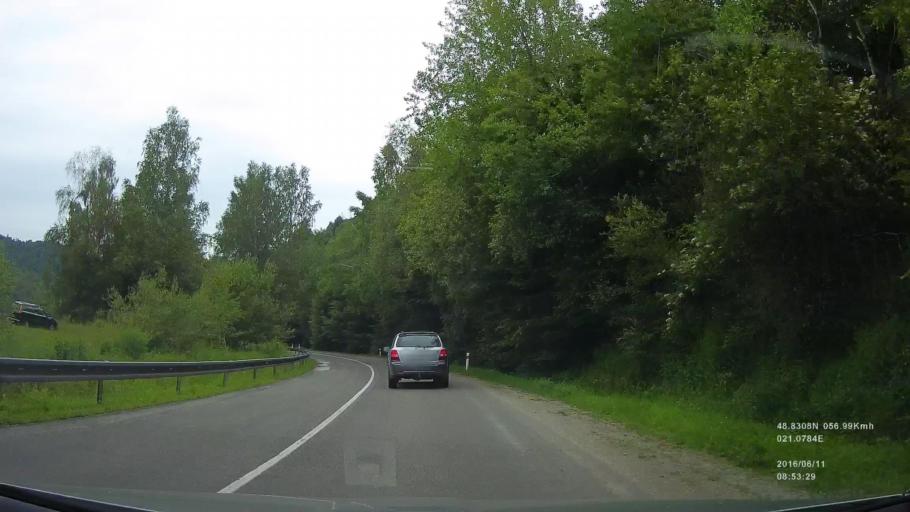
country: SK
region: Kosicky
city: Kosice
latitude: 48.7930
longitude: 21.1204
